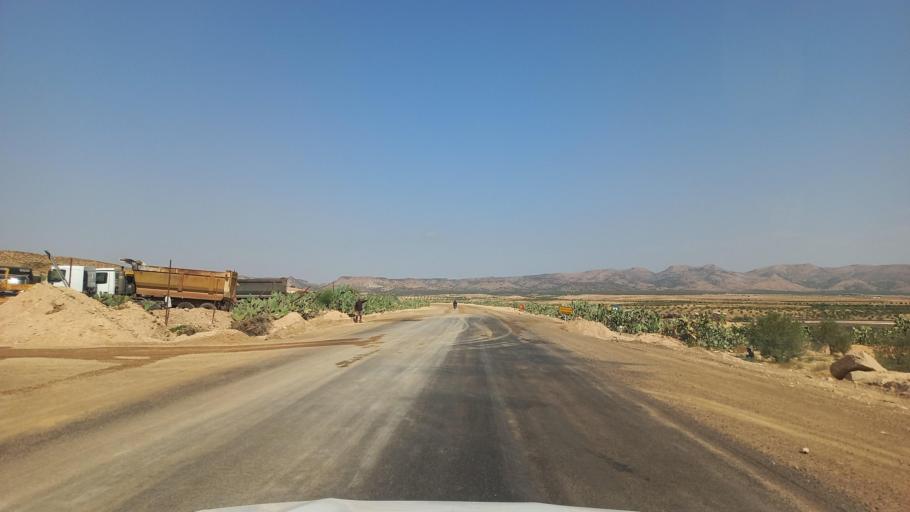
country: TN
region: Al Qasrayn
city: Sbiba
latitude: 35.3814
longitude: 9.0293
